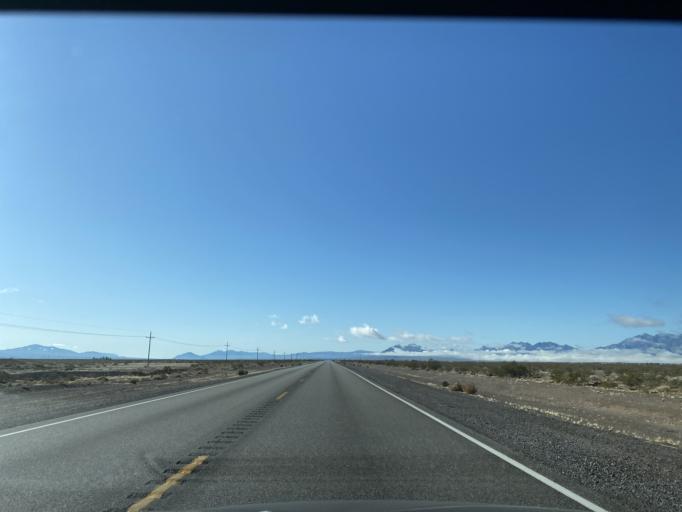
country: US
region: Nevada
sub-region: Nye County
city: Beatty
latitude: 36.5928
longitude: -116.4095
